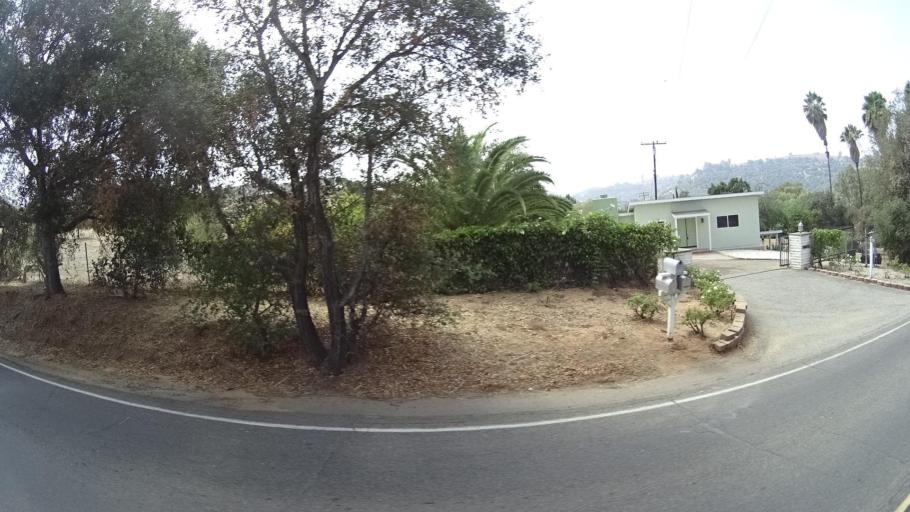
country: US
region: California
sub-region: San Diego County
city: Rainbow
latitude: 33.3712
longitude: -117.1739
